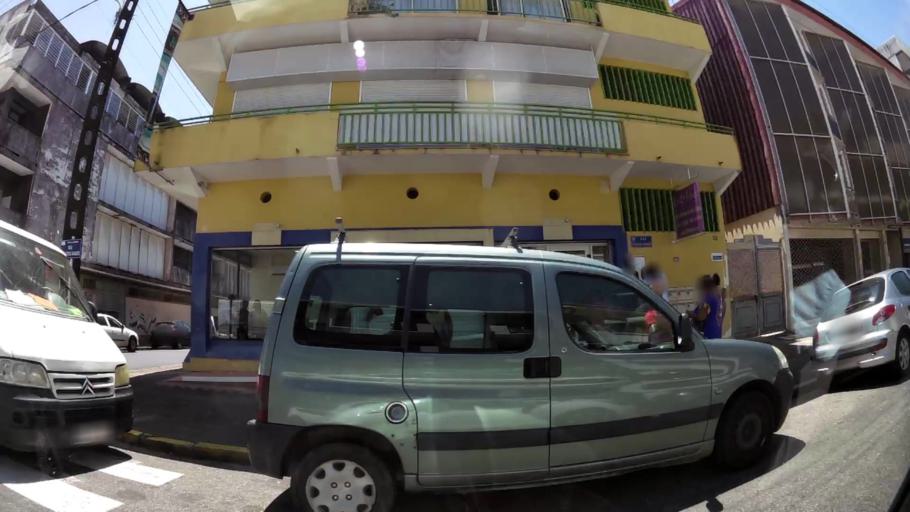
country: GF
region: Guyane
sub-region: Guyane
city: Cayenne
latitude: 4.9407
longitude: -52.3322
